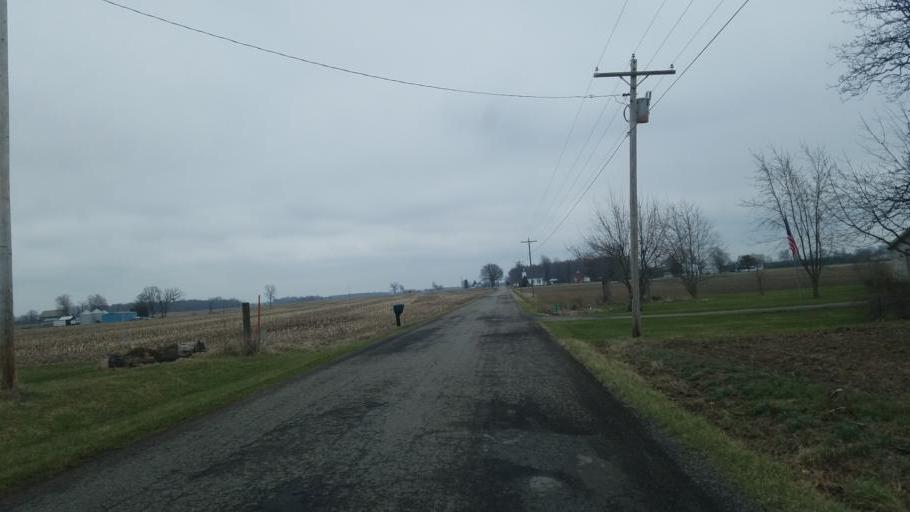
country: US
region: Ohio
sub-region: Morrow County
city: Mount Gilead
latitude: 40.6308
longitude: -82.9234
